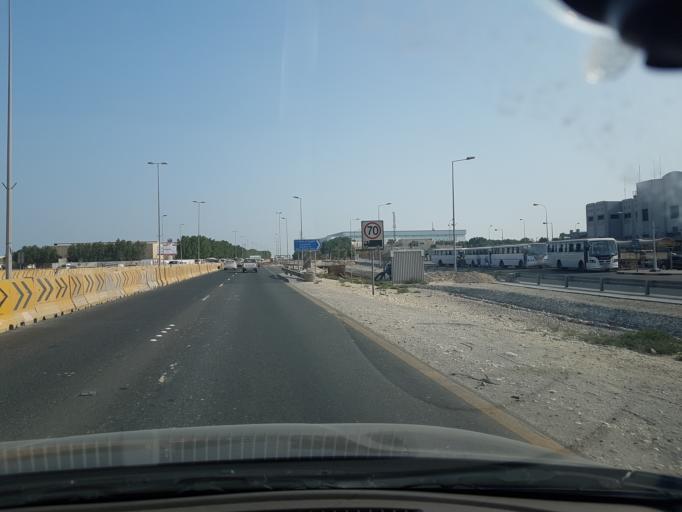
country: BH
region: Northern
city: Sitrah
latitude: 26.0866
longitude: 50.6115
